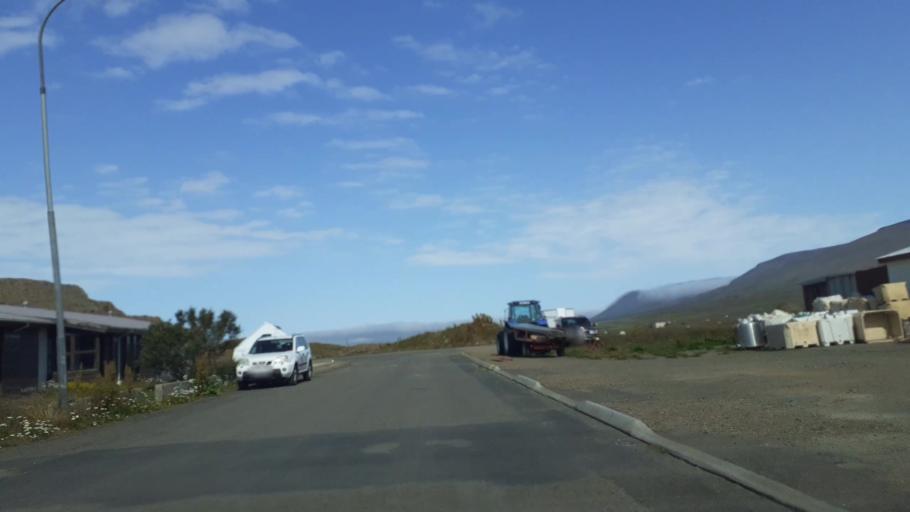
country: IS
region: Northwest
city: Saudarkrokur
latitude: 65.8283
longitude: -20.3162
